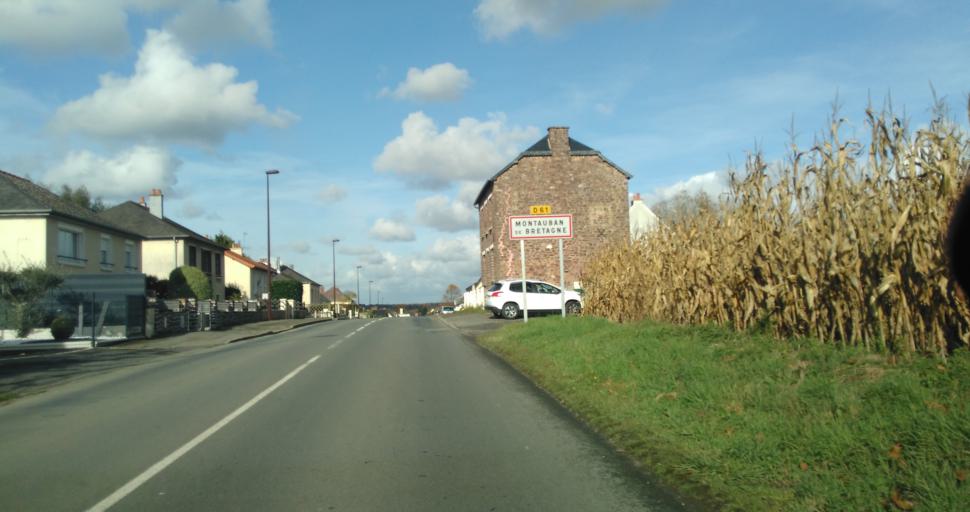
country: FR
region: Brittany
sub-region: Departement d'Ille-et-Vilaine
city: Montauban-de-Bretagne
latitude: 48.1853
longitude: -2.0502
